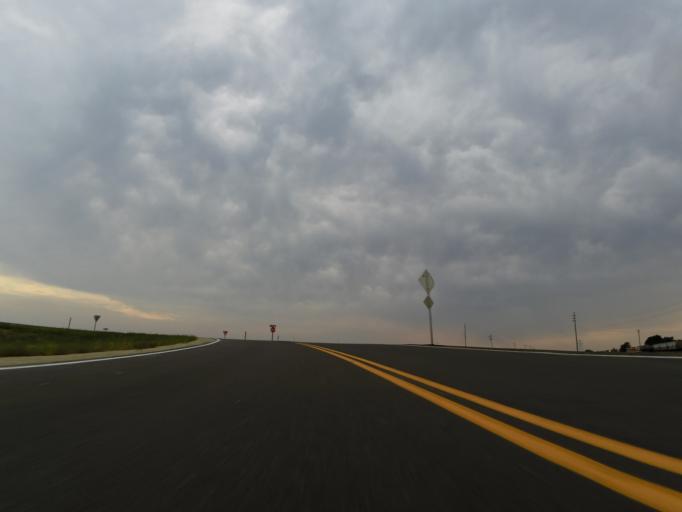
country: US
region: Kansas
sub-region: Reno County
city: South Hutchinson
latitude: 38.0139
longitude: -98.0022
